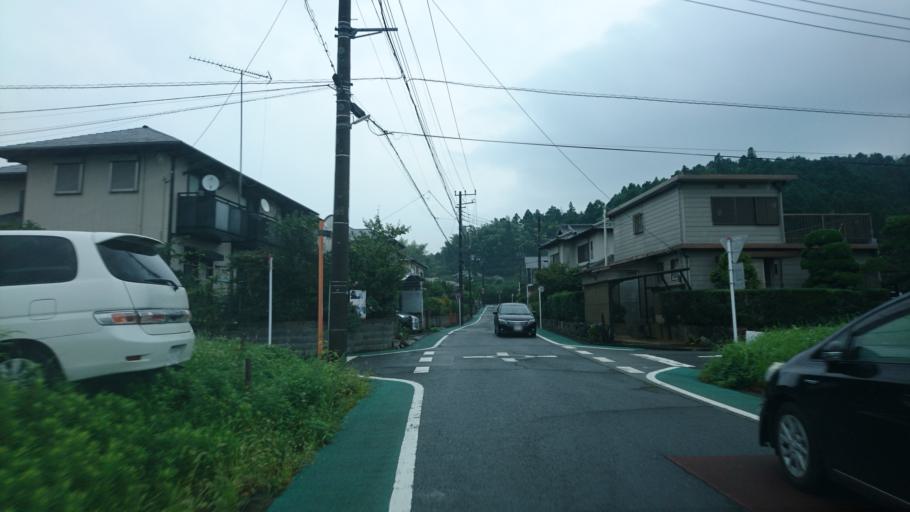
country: JP
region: Chiba
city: Kimitsu
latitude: 35.3033
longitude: 139.9580
